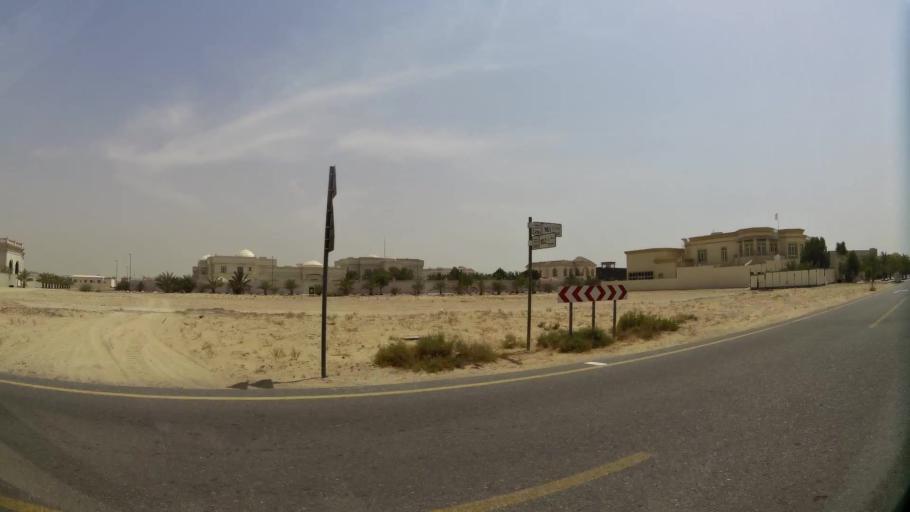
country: AE
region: Ash Shariqah
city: Sharjah
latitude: 25.2573
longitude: 55.4860
